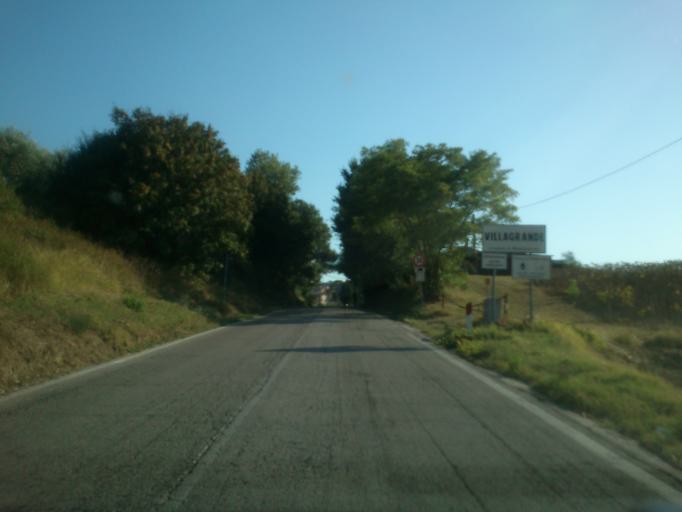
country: IT
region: The Marches
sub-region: Provincia di Pesaro e Urbino
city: Mombaroccio
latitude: 43.8125
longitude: 12.8611
